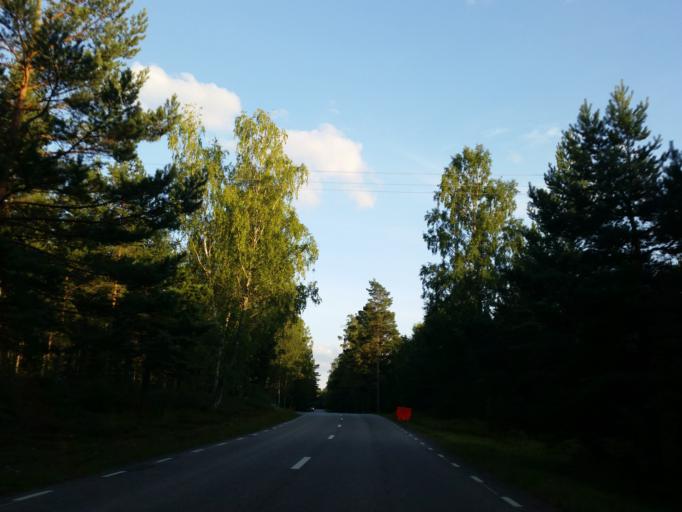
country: SE
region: Stockholm
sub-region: Sodertalje Kommun
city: Soedertaelje
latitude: 59.2403
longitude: 17.5429
